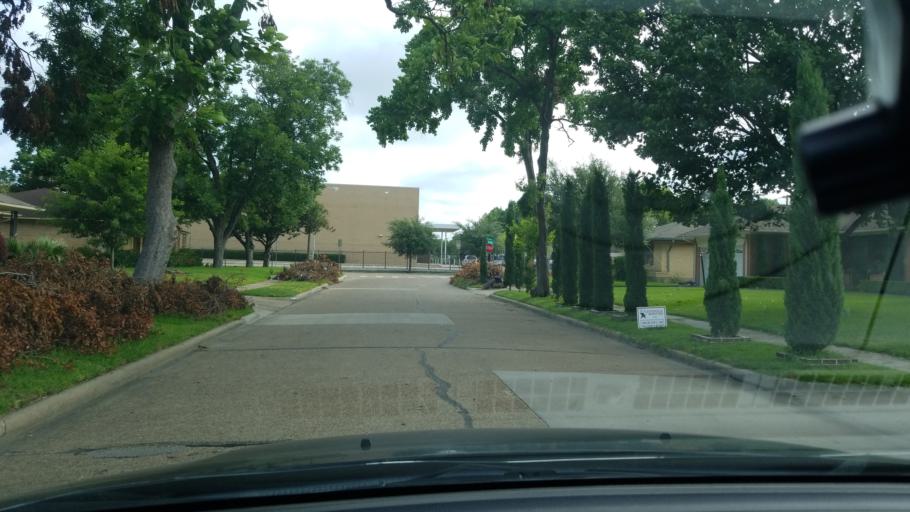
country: US
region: Texas
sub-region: Dallas County
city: Mesquite
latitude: 32.8173
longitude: -96.6807
